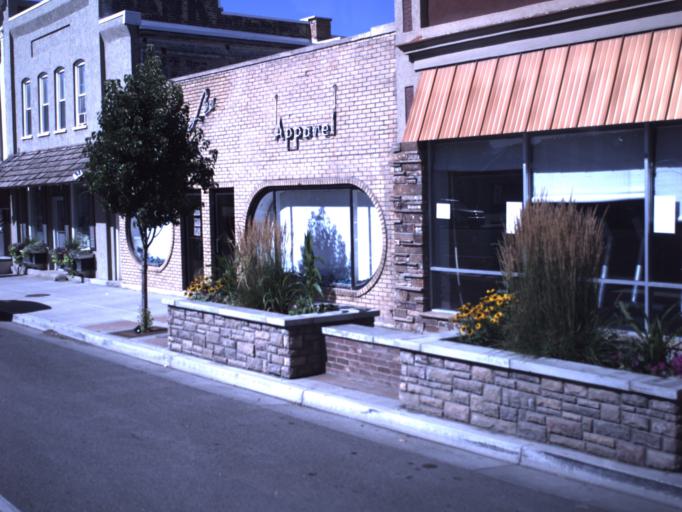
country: US
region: Utah
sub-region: Sanpete County
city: Gunnison
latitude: 39.1543
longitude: -111.8184
